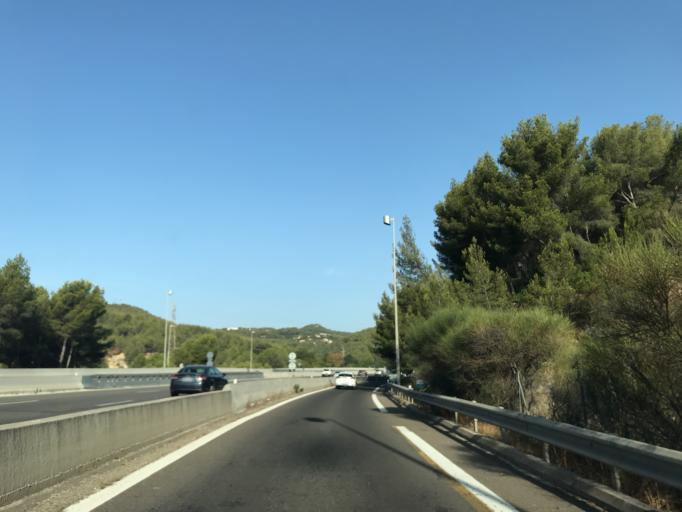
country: FR
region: Provence-Alpes-Cote d'Azur
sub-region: Departement du Var
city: Bandol
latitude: 43.1471
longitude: 5.7697
